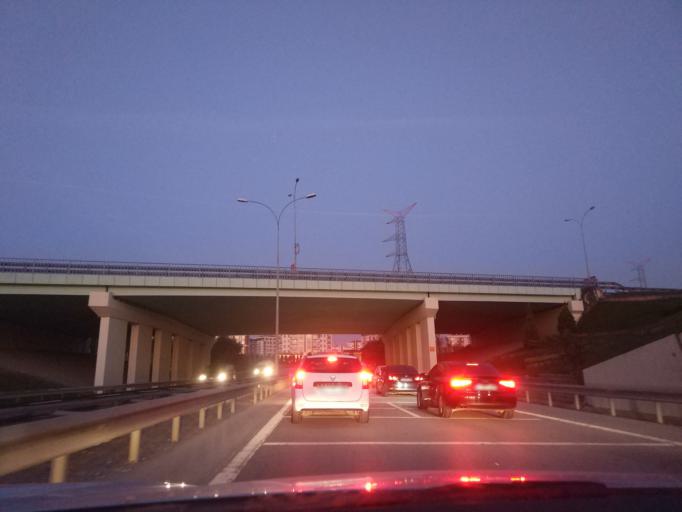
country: TR
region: Istanbul
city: Pendik
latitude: 40.9146
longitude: 29.3132
